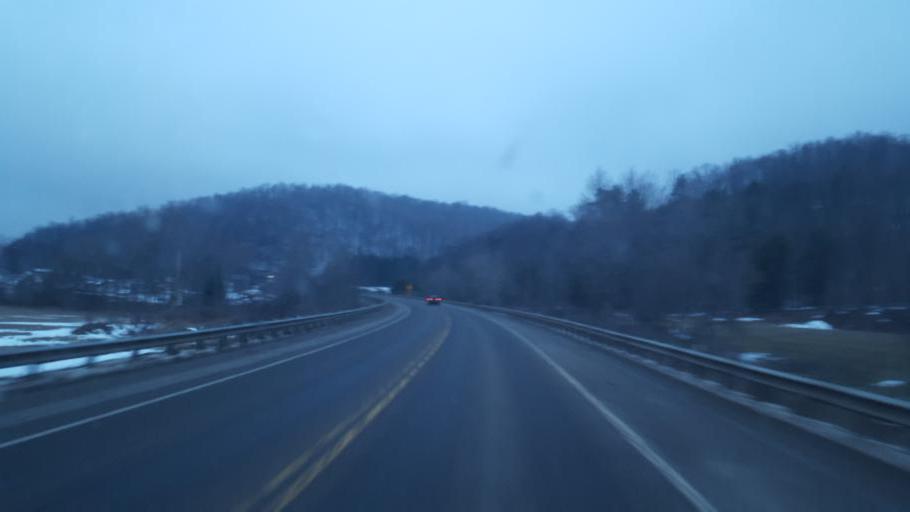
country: US
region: Pennsylvania
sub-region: Potter County
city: Coudersport
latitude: 41.7752
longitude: -78.1309
